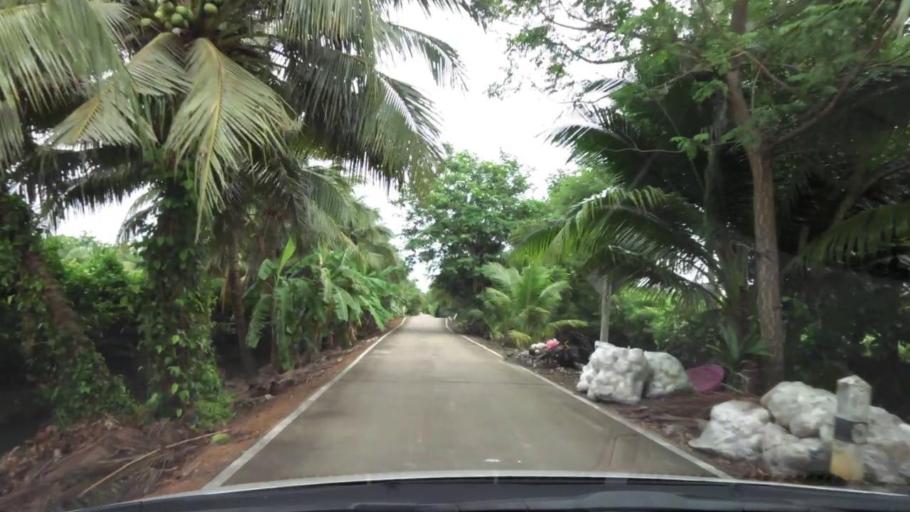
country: TH
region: Ratchaburi
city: Damnoen Saduak
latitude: 13.5535
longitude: 99.9842
